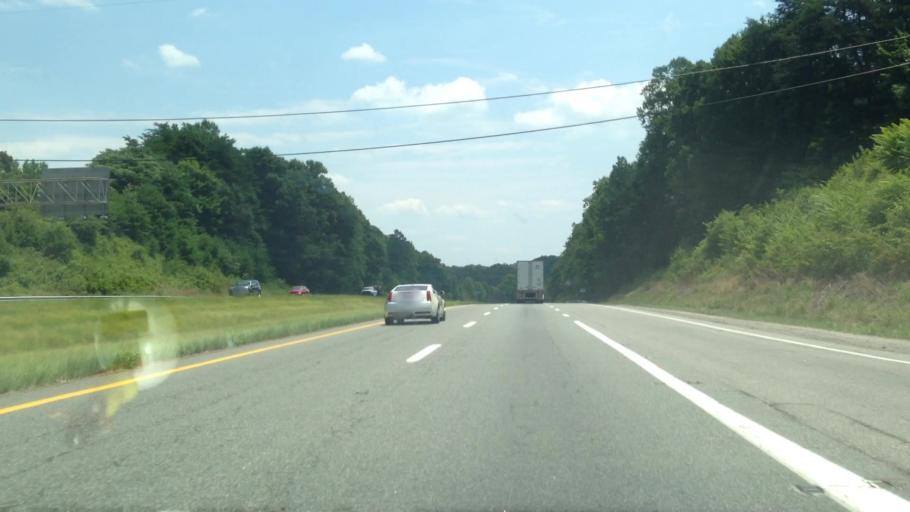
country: US
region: Virginia
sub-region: Henry County
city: Horse Pasture
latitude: 36.6474
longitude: -79.9115
